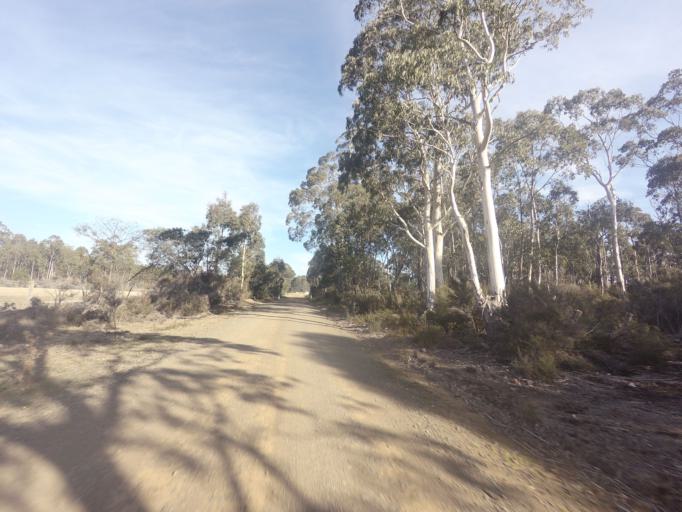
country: AU
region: Tasmania
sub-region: Sorell
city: Sorell
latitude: -42.5070
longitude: 147.4777
